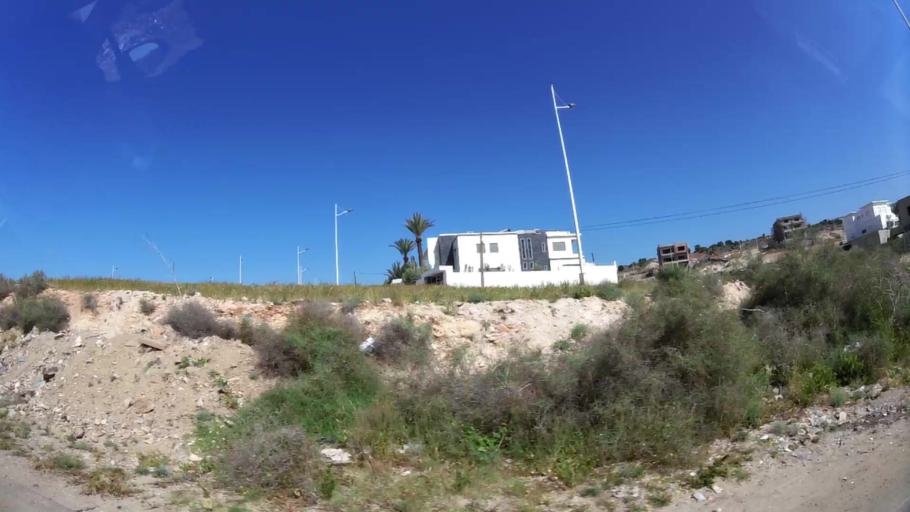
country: MA
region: Souss-Massa-Draa
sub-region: Agadir-Ida-ou-Tnan
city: Agadir
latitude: 30.4419
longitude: -9.5781
